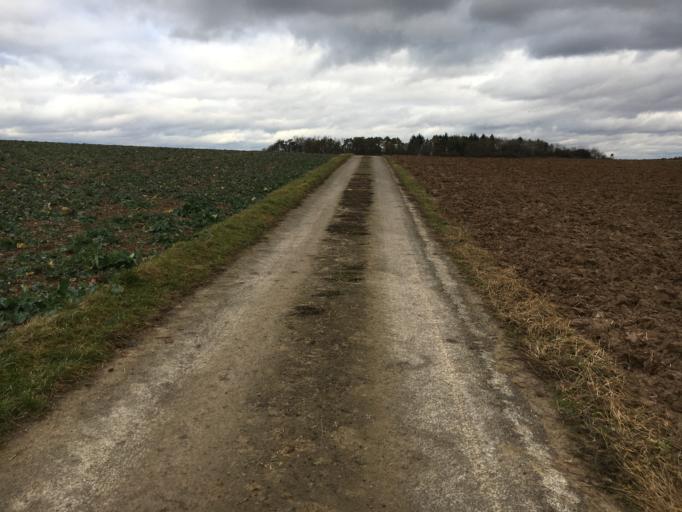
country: DE
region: Baden-Wuerttemberg
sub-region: Karlsruhe Region
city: Mosbach
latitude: 49.3730
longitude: 9.2008
